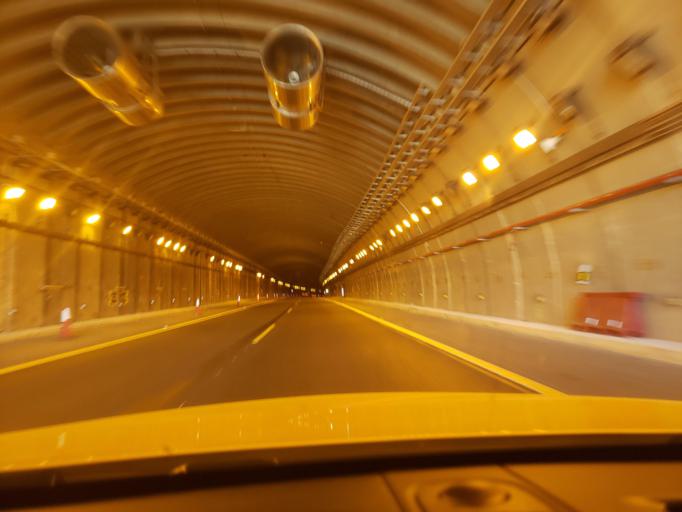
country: ES
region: Andalusia
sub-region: Provincia de Malaga
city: Fuengirola
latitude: 36.5049
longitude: -4.7305
